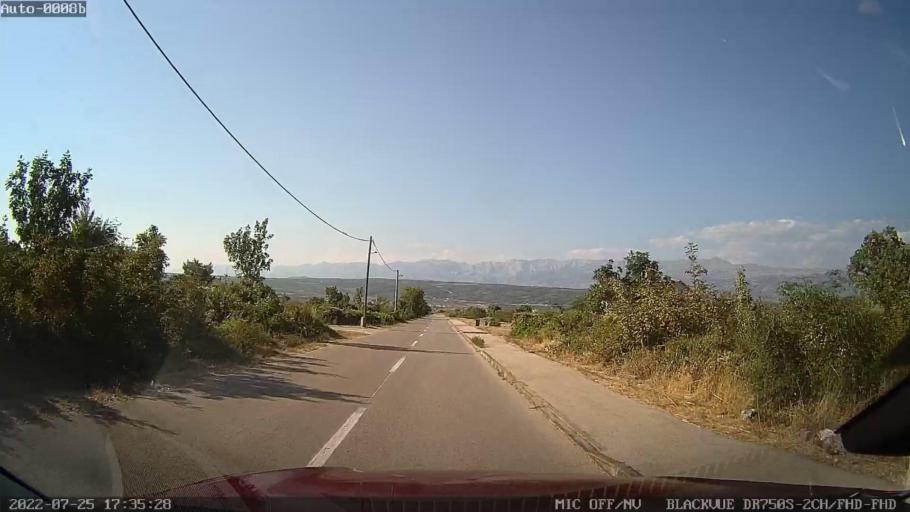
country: HR
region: Zadarska
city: Posedarje
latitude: 44.1911
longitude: 15.4727
